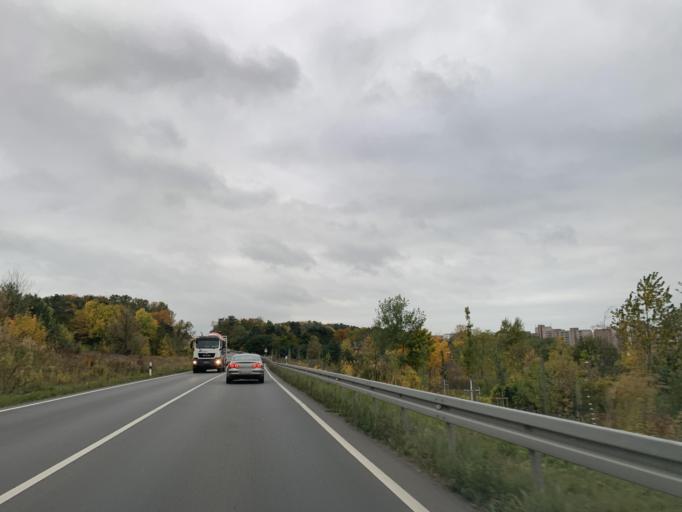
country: DE
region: Mecklenburg-Vorpommern
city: Neubrandenburg
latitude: 53.5463
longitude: 13.2747
